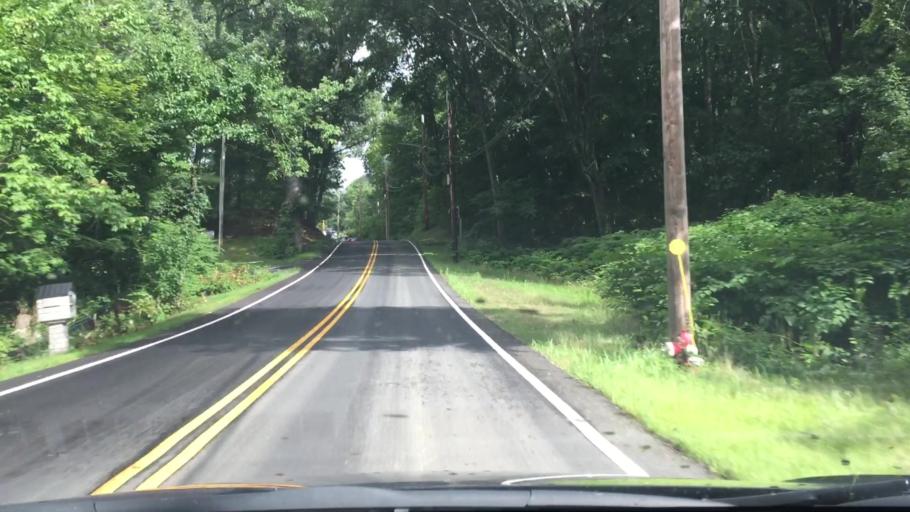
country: US
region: Massachusetts
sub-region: Middlesex County
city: Littleton Common
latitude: 42.5222
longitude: -71.4586
